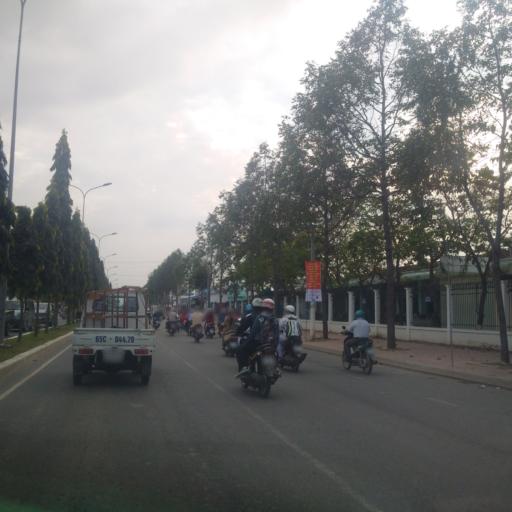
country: VN
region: Can Tho
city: Can Tho
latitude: 10.0344
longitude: 105.7561
